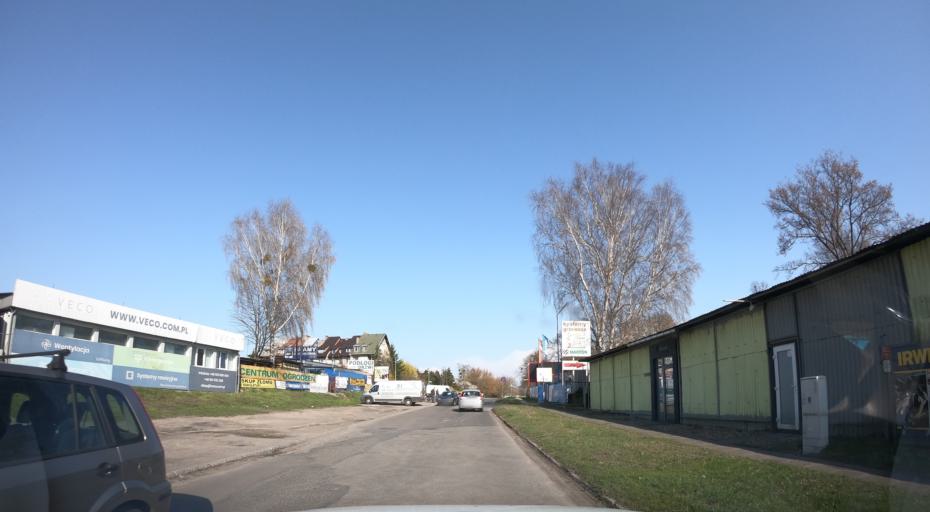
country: PL
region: West Pomeranian Voivodeship
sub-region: Szczecin
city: Szczecin
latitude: 53.4252
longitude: 14.5025
